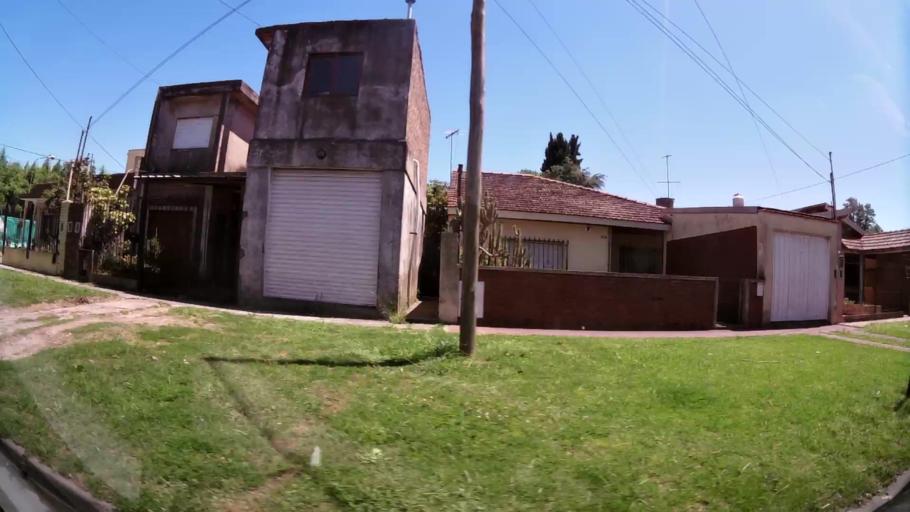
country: AR
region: Buenos Aires
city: Hurlingham
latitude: -34.5013
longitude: -58.6319
